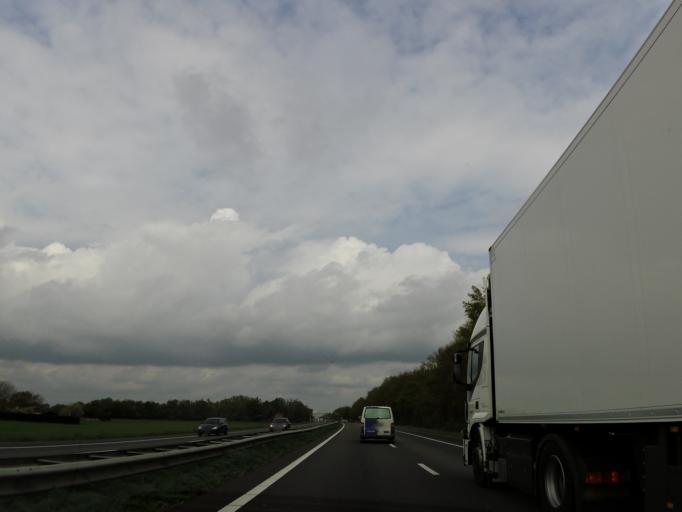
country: NL
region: Limburg
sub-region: Gemeente Leudal
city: Kelpen-Oler
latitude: 51.1864
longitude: 5.8419
